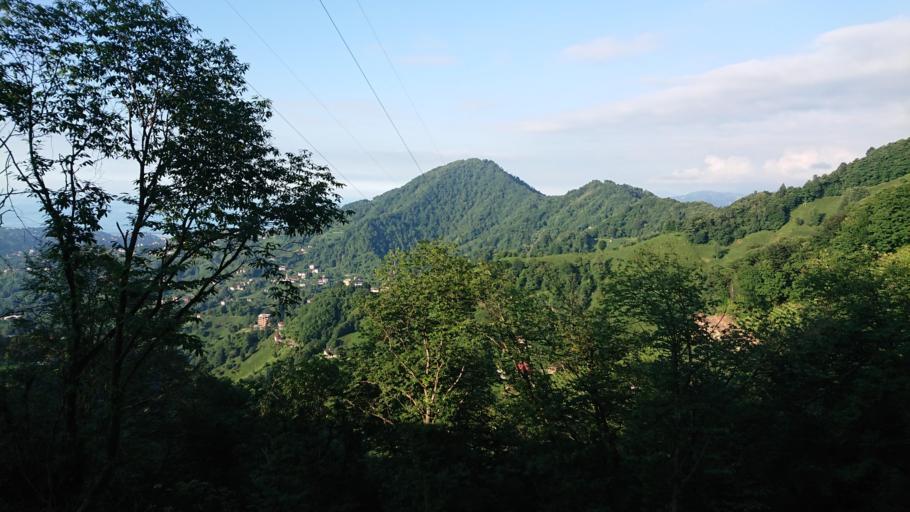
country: TR
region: Rize
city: Rize
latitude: 40.9695
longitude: 40.4836
